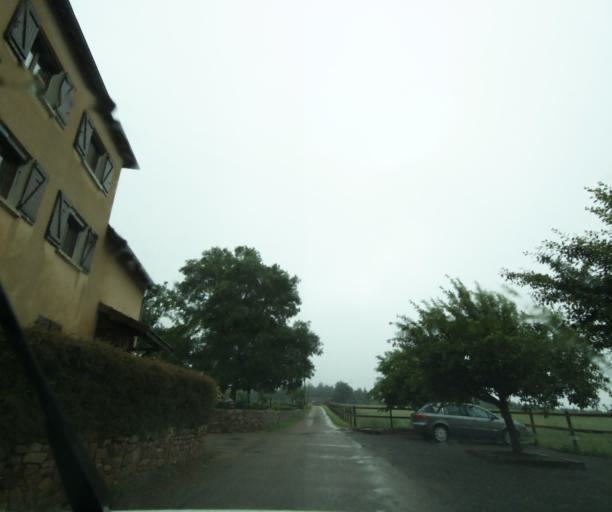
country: FR
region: Bourgogne
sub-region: Departement de Saone-et-Loire
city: Charolles
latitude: 46.3900
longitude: 4.3712
